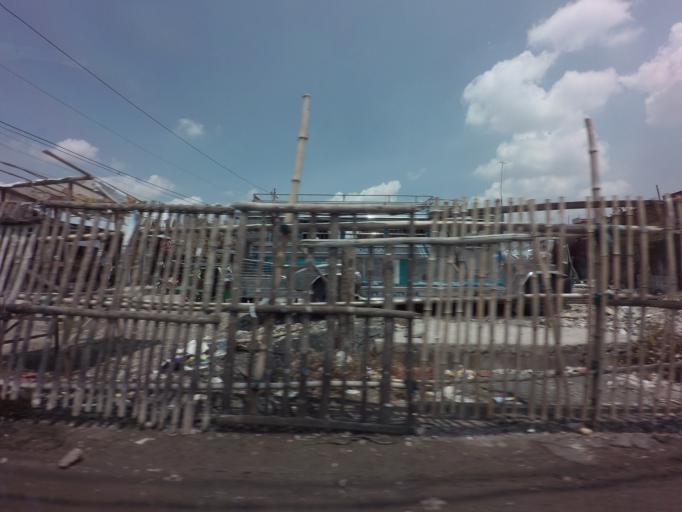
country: PH
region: Calabarzon
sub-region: Province of Laguna
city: San Pedro
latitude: 14.4072
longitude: 121.0500
